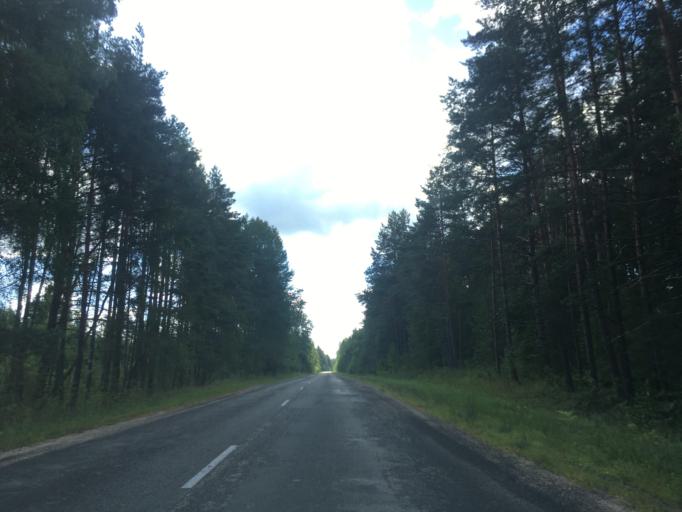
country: RU
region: Pskov
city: Pskov
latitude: 57.7130
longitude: 28.1734
